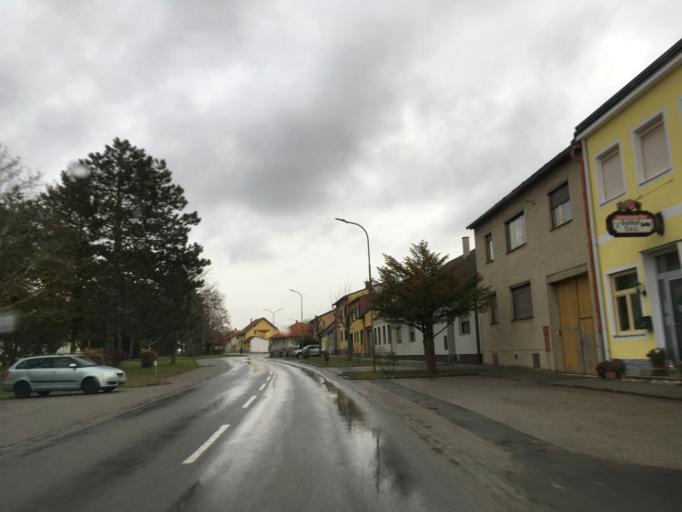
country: AT
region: Lower Austria
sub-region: Politischer Bezirk Wien-Umgebung
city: Rauchenwarth
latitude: 48.0832
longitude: 16.5315
